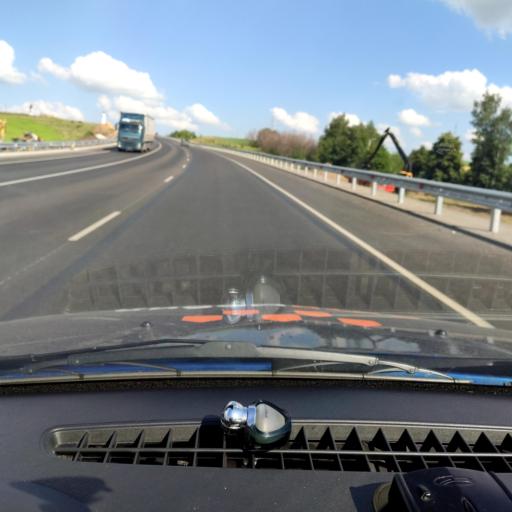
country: RU
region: Lipetsk
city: Yelets
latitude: 52.5791
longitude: 38.5166
